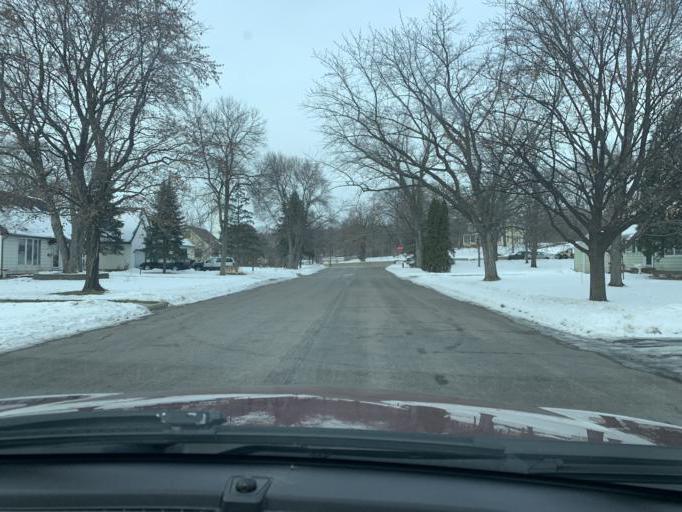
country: US
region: Minnesota
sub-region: Washington County
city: Saint Paul Park
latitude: 44.8450
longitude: -92.9870
